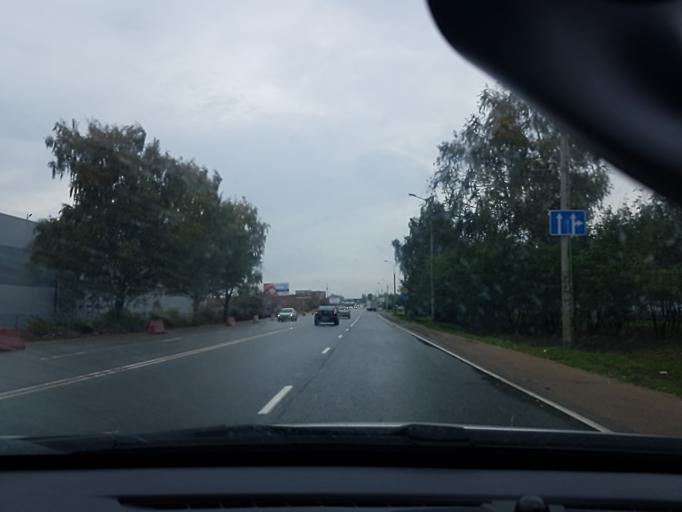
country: RU
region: Moskovskaya
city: Pavlovskaya Sloboda
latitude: 55.8148
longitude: 37.0619
